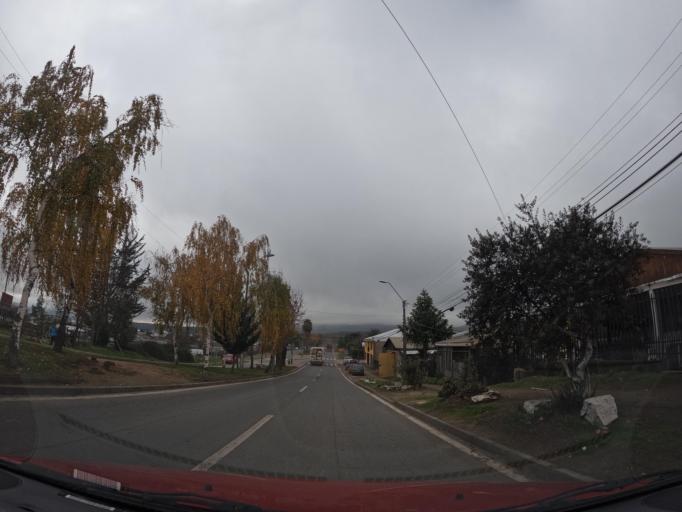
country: CL
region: Maule
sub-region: Provincia de Cauquenes
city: Cauquenes
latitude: -36.2784
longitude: -72.5422
